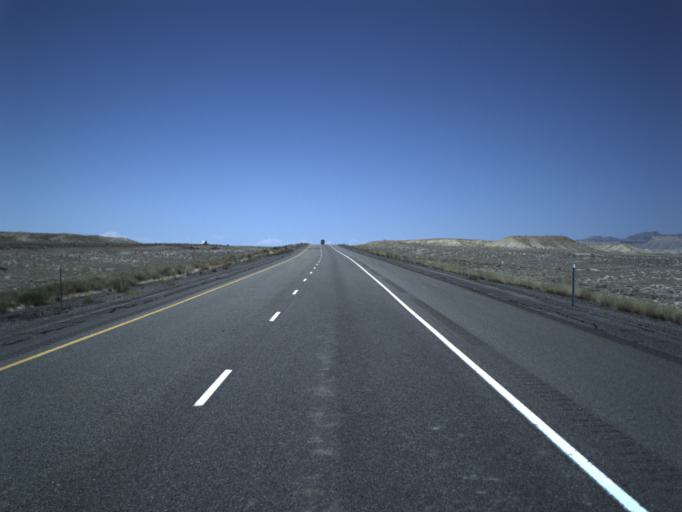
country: US
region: Utah
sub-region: Grand County
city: Moab
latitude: 38.9427
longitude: -109.5322
